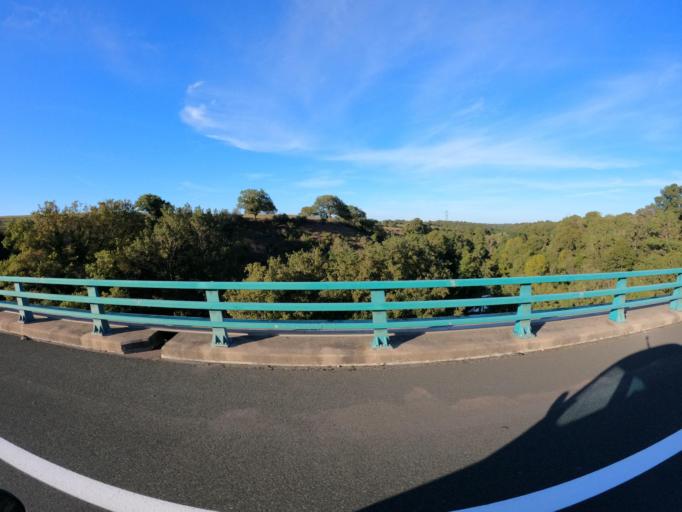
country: FR
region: Pays de la Loire
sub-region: Departement de Maine-et-Loire
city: Chemille-Melay
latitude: 47.2439
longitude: -0.6725
